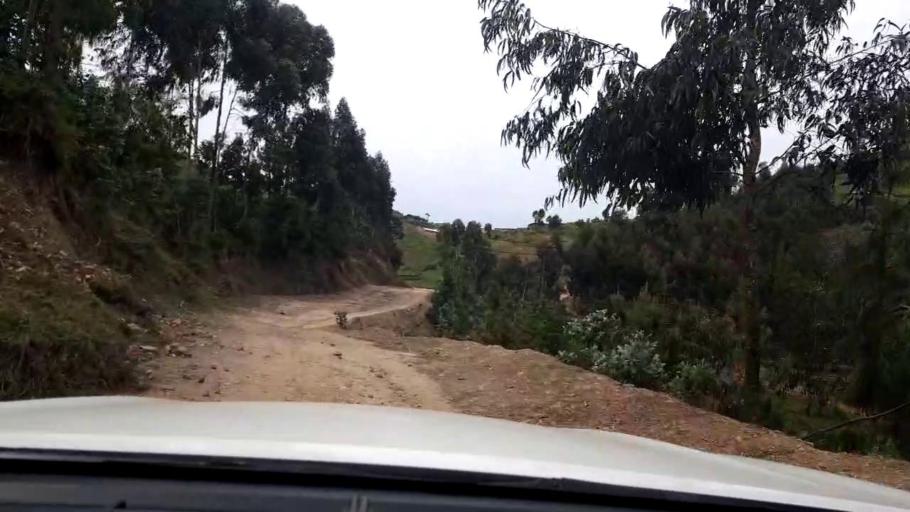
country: RW
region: Western Province
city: Kibuye
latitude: -1.8881
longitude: 29.4532
